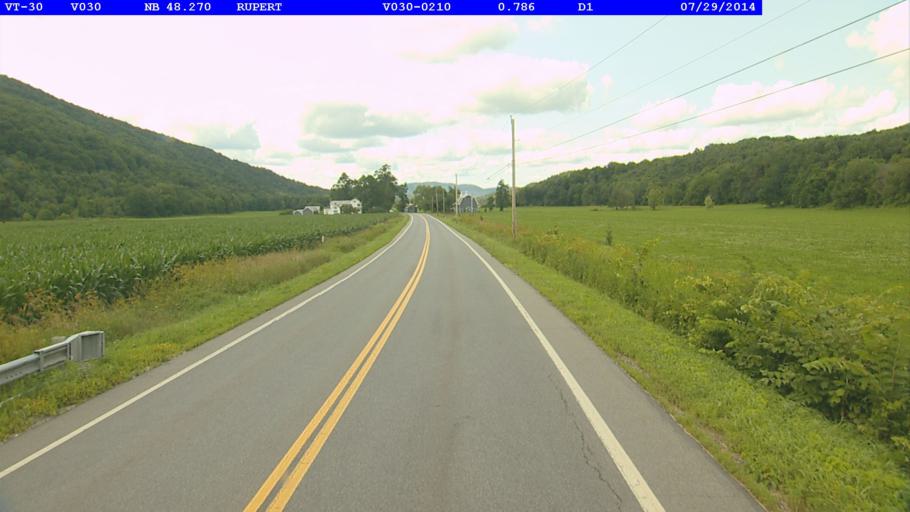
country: US
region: Vermont
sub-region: Bennington County
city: Manchester Center
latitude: 43.2819
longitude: -73.1266
